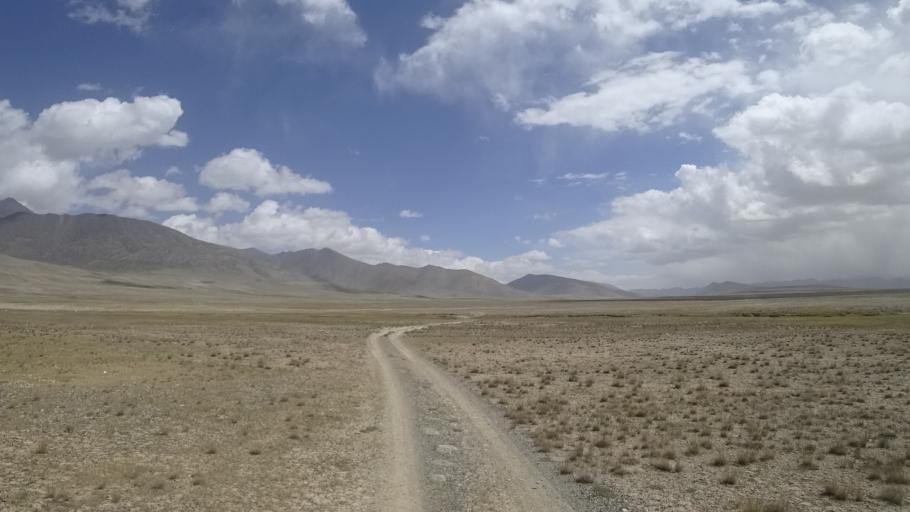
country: TJ
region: Gorno-Badakhshan
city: Murghob
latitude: 37.4760
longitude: 73.9740
